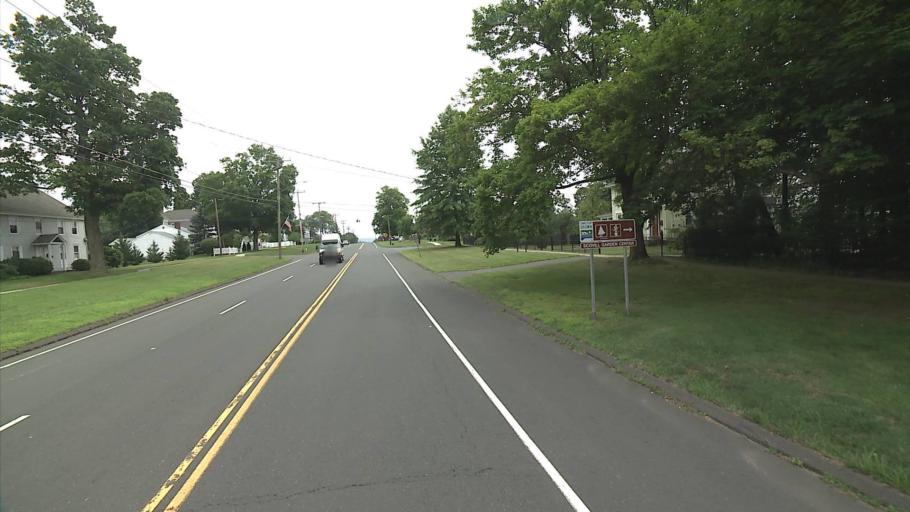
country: US
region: Connecticut
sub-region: Middlesex County
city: Cromwell
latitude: 41.6026
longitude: -72.6466
